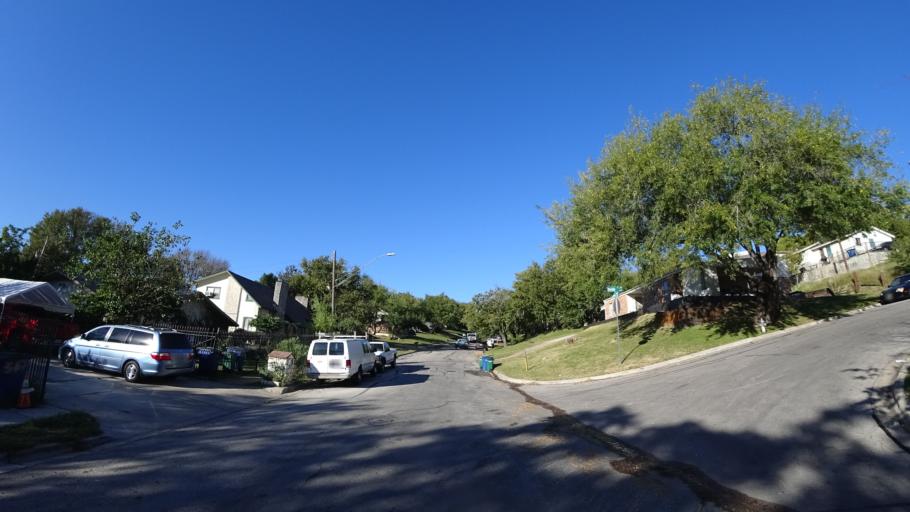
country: US
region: Texas
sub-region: Travis County
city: Austin
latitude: 30.3057
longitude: -97.6711
